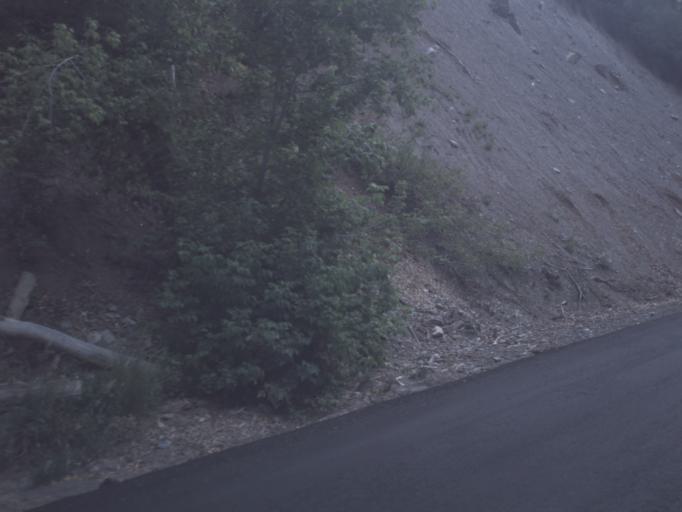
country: US
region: Utah
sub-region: Utah County
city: Cedar Hills
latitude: 40.4506
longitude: -111.6535
